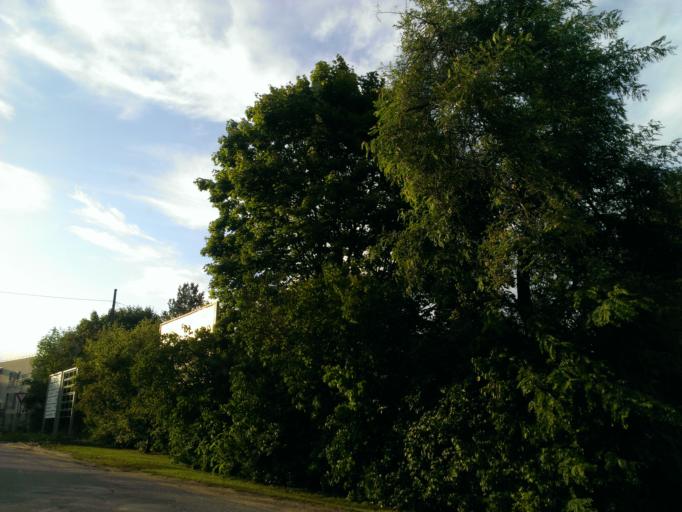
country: LV
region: Ikskile
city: Ikskile
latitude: 56.8422
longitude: 24.5027
